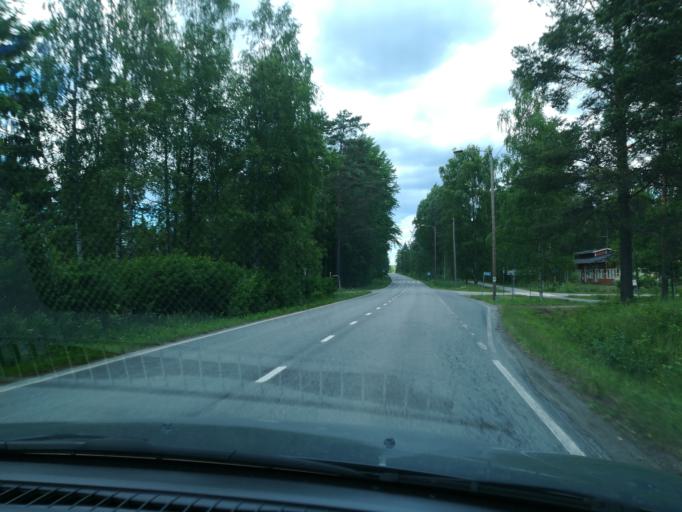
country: FI
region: Southern Savonia
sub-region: Mikkeli
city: Hirvensalmi
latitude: 61.6522
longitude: 26.7702
